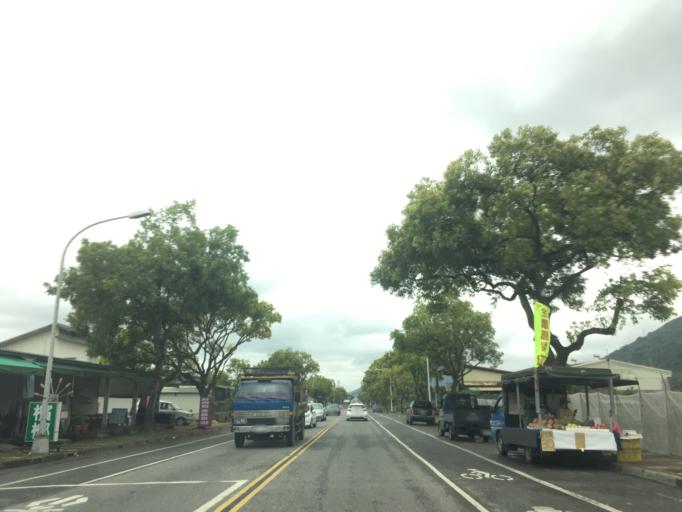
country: TW
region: Taiwan
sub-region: Hualien
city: Hualian
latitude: 23.9778
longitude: 121.5661
